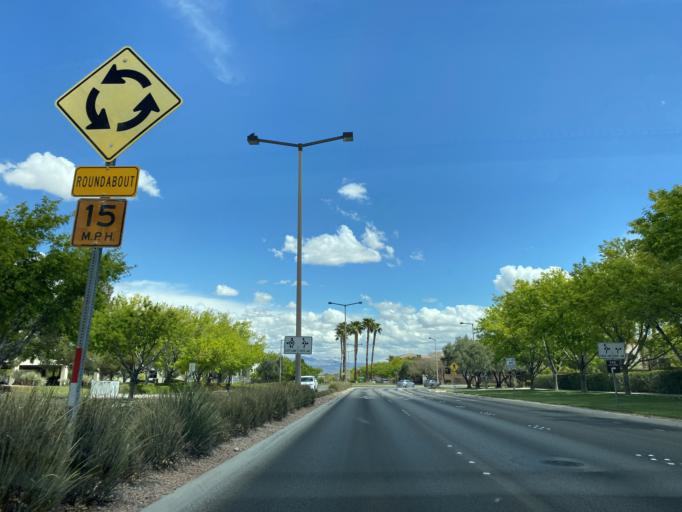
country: US
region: Nevada
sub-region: Clark County
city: Summerlin South
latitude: 36.1800
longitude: -115.3149
